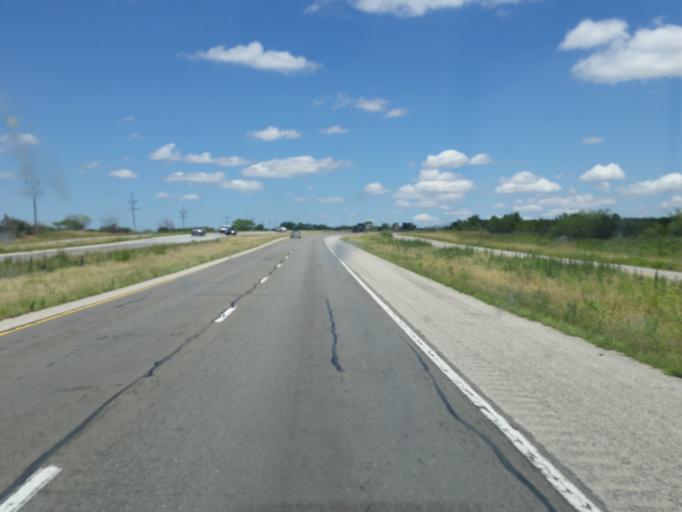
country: US
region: Texas
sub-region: Nolan County
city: Sweetwater
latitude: 32.4961
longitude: -100.2710
